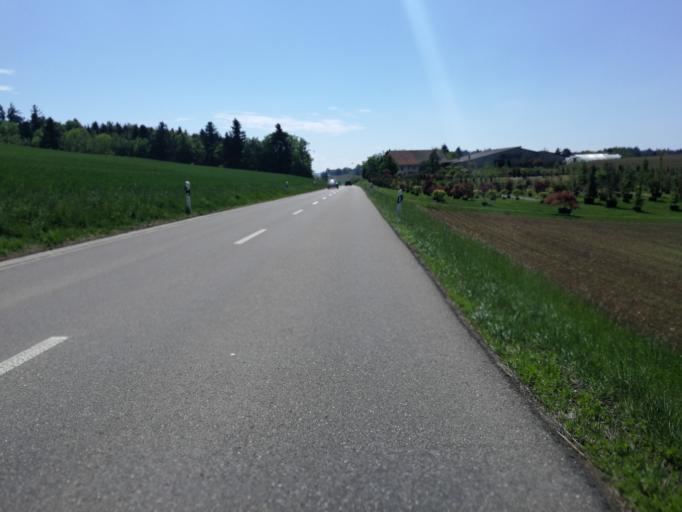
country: CH
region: Zurich
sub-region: Bezirk Uster
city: Aesch
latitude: 47.3141
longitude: 8.6413
